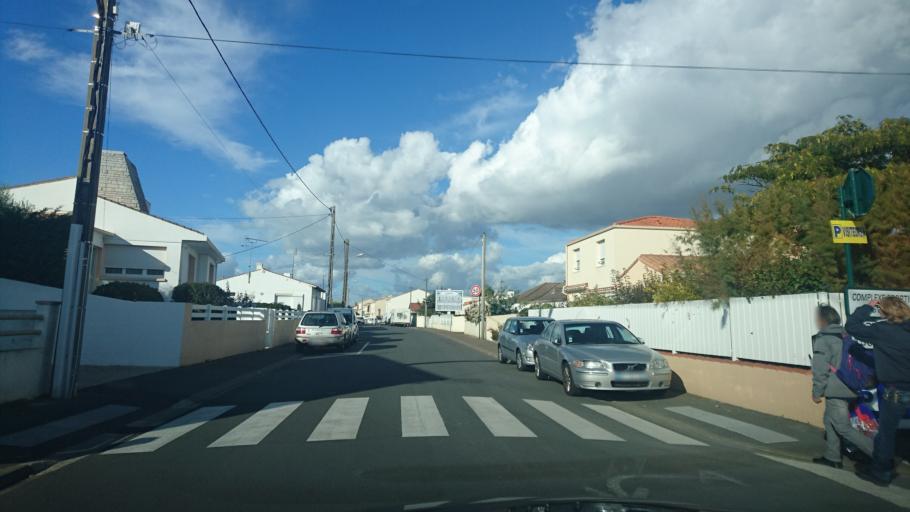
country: FR
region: Pays de la Loire
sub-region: Departement de la Vendee
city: Les Sables-d'Olonne
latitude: 46.5050
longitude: -1.8003
